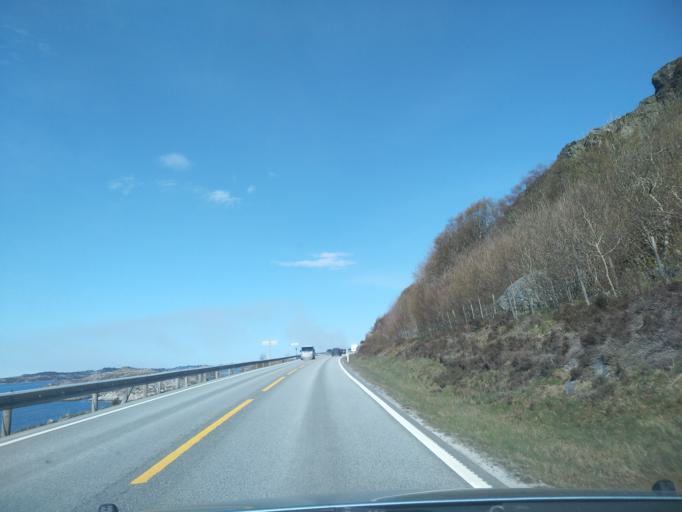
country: NO
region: Rogaland
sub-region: Bokn
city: Bokn
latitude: 59.2568
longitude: 5.4646
